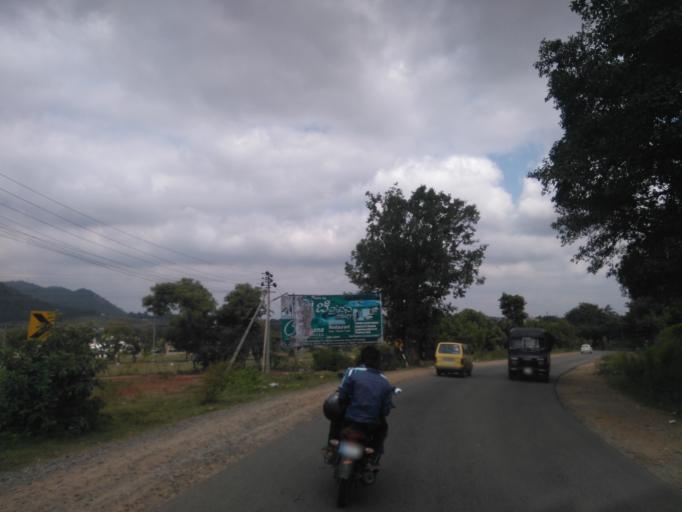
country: IN
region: Karnataka
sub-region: Mysore
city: Mysore
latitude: 12.2899
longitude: 76.7103
